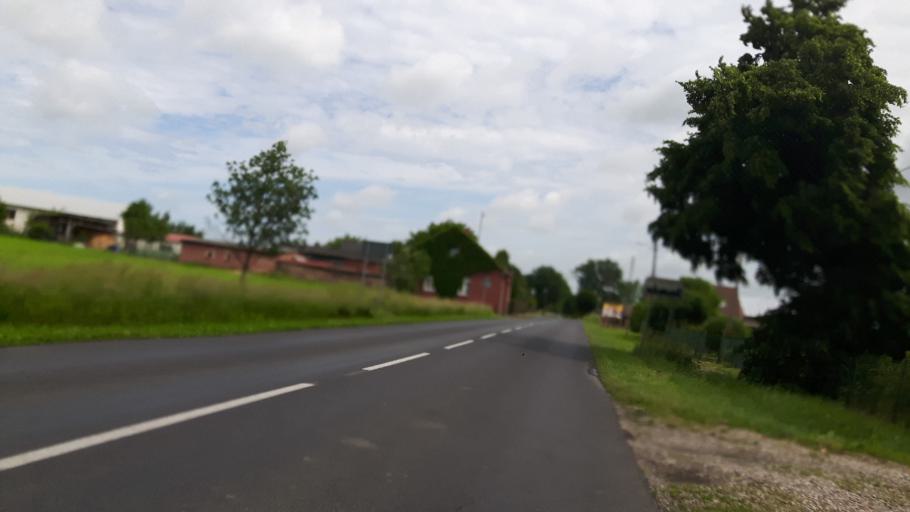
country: PL
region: West Pomeranian Voivodeship
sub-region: Powiat gryficki
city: Trzebiatow
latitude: 54.0079
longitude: 15.2431
